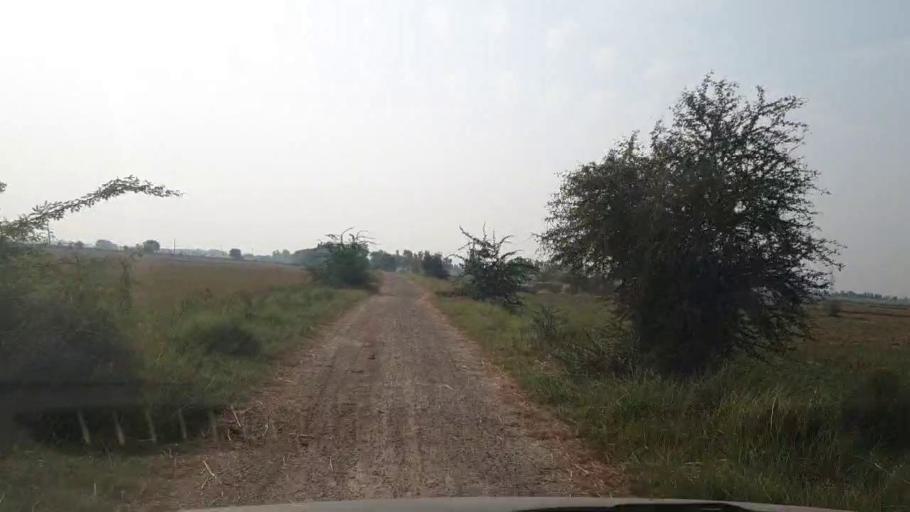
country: PK
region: Sindh
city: Tando Muhammad Khan
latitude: 25.1010
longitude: 68.5019
